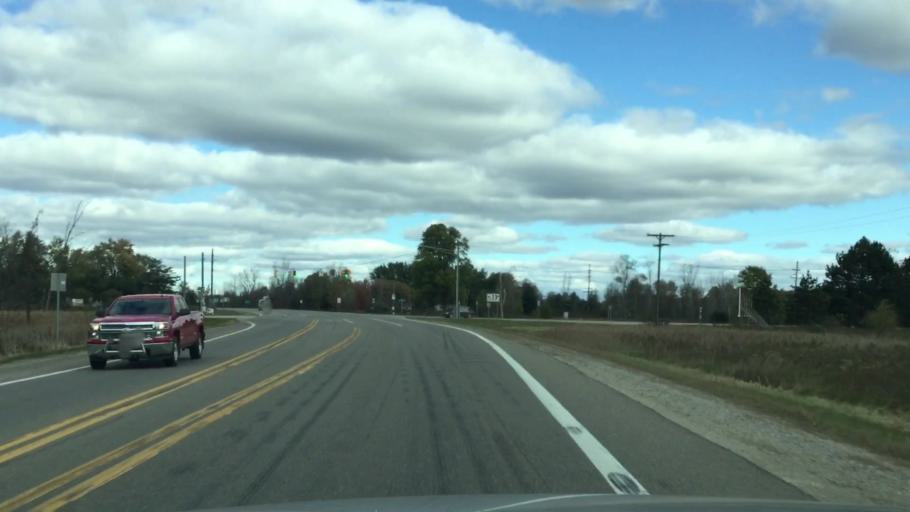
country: US
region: Michigan
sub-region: Lapeer County
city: Barnes Lake-Millers Lake
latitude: 43.2181
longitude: -83.3141
